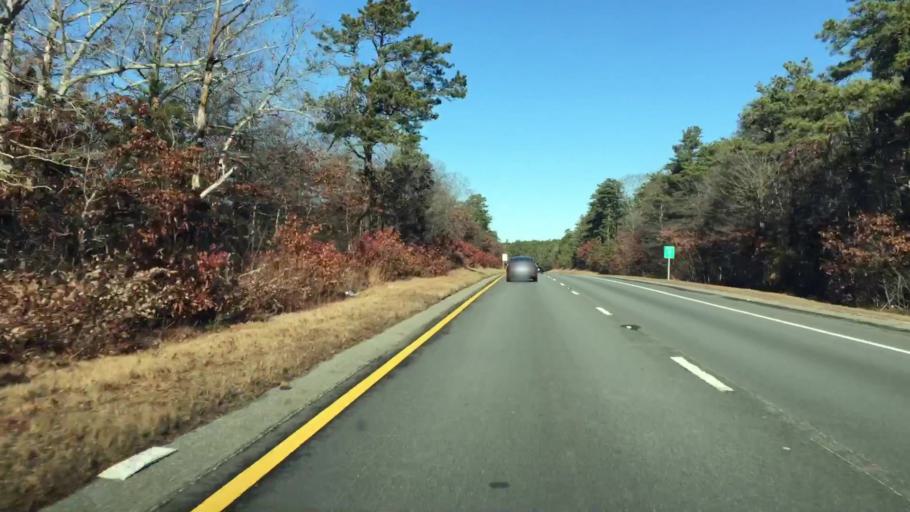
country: US
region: Massachusetts
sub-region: Barnstable County
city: Monument Beach
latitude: 41.7069
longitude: -70.5834
